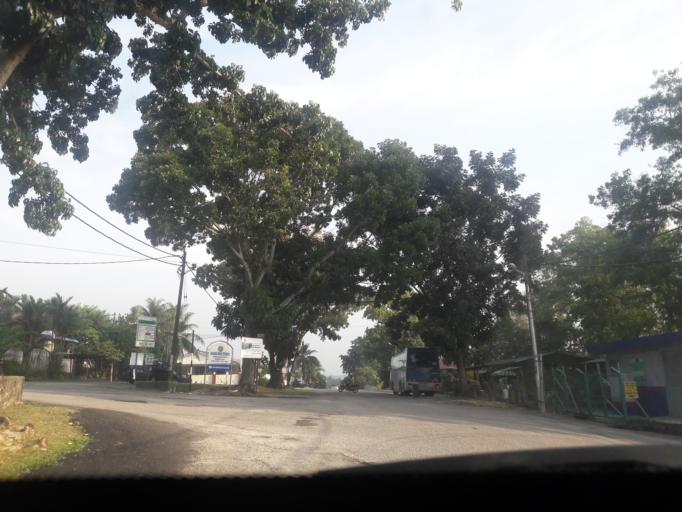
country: MY
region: Kedah
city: Kulim
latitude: 5.3773
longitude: 100.5364
